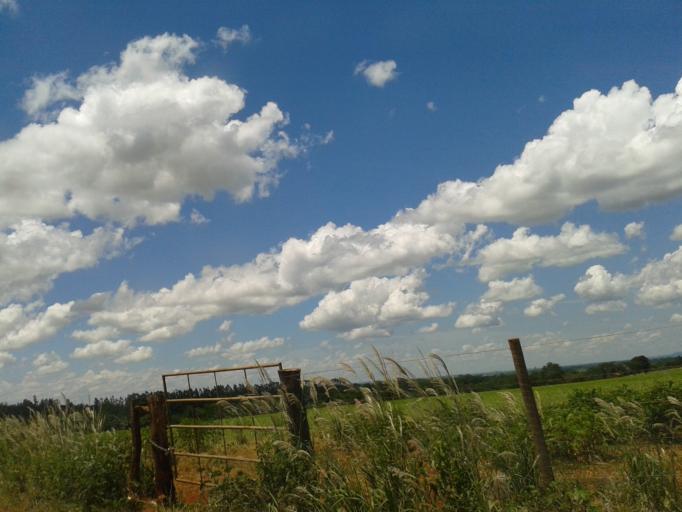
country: BR
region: Minas Gerais
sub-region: Centralina
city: Centralina
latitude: -18.6967
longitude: -49.1643
